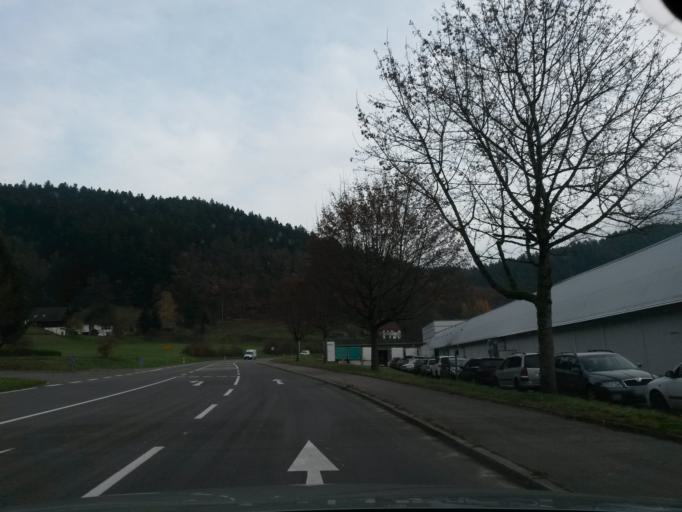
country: DE
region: Baden-Wuerttemberg
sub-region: Freiburg Region
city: Schenkenzell
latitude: 48.3147
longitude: 8.3788
